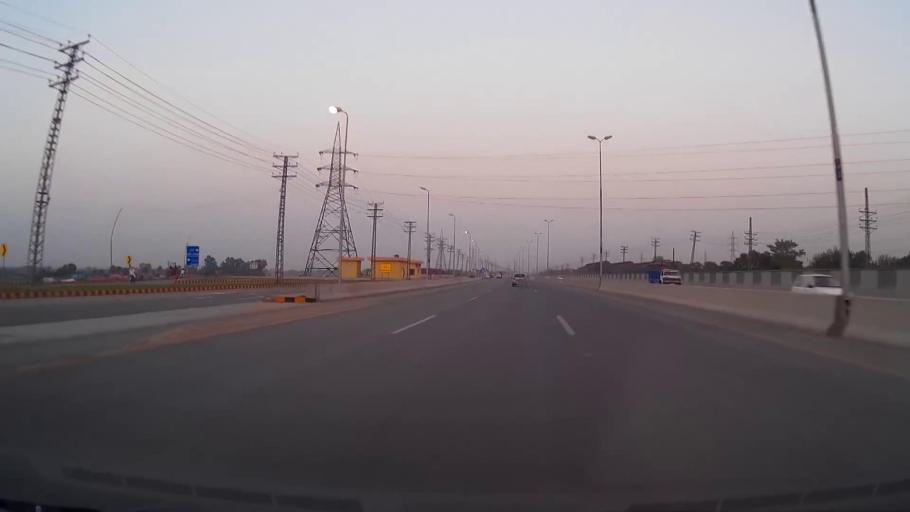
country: PK
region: Punjab
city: Lahore
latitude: 31.6096
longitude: 74.3226
